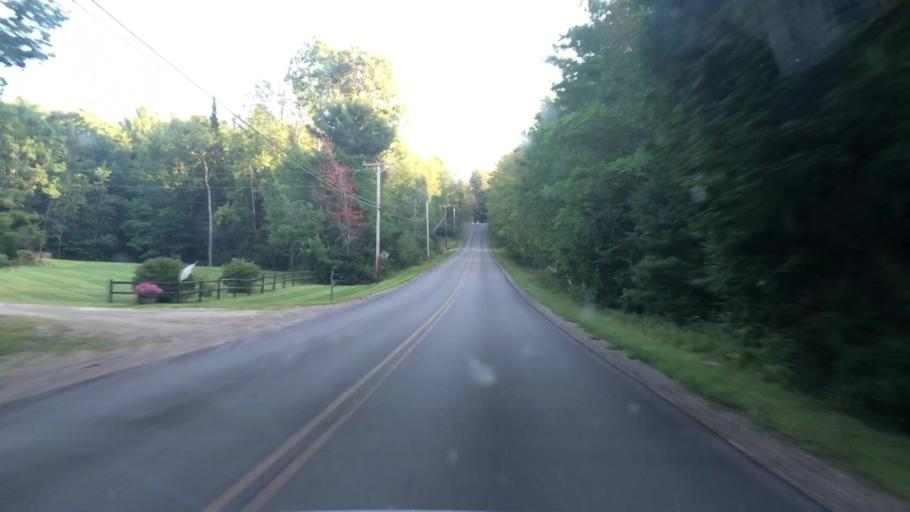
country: US
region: Maine
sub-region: Penobscot County
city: Hampden
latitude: 44.7148
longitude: -68.8869
